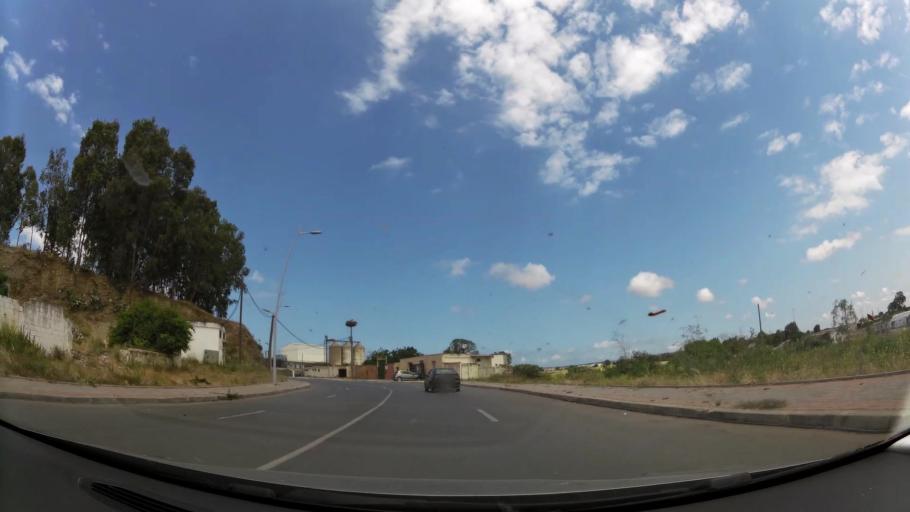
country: MA
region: Gharb-Chrarda-Beni Hssen
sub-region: Kenitra Province
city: Kenitra
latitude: 34.2765
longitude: -6.5921
